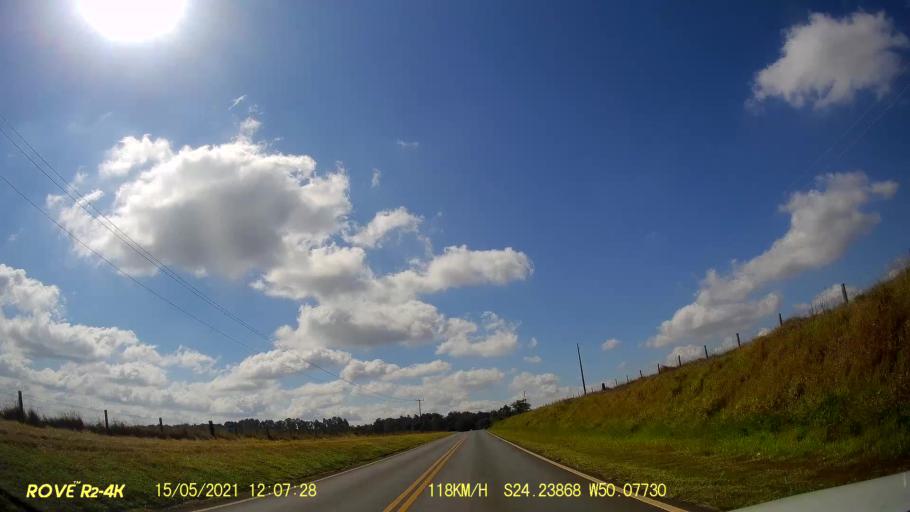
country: BR
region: Parana
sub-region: Pirai Do Sul
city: Pirai do Sul
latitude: -24.2388
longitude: -50.0775
